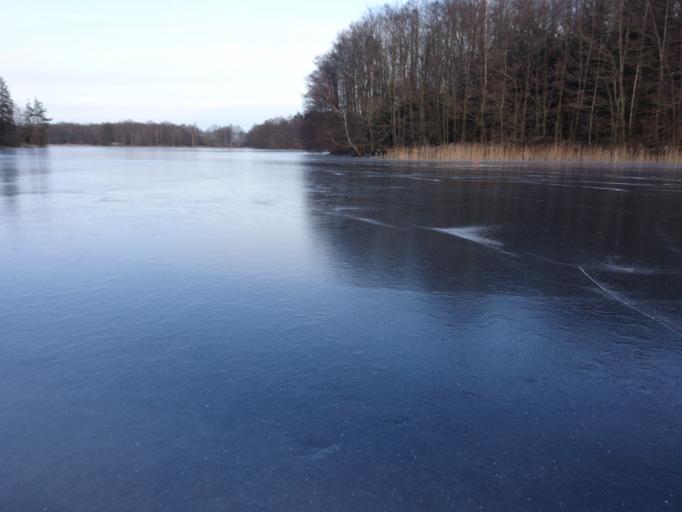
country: SE
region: Blekinge
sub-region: Karlshamns Kommun
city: Karlshamn
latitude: 56.2335
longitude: 14.9653
